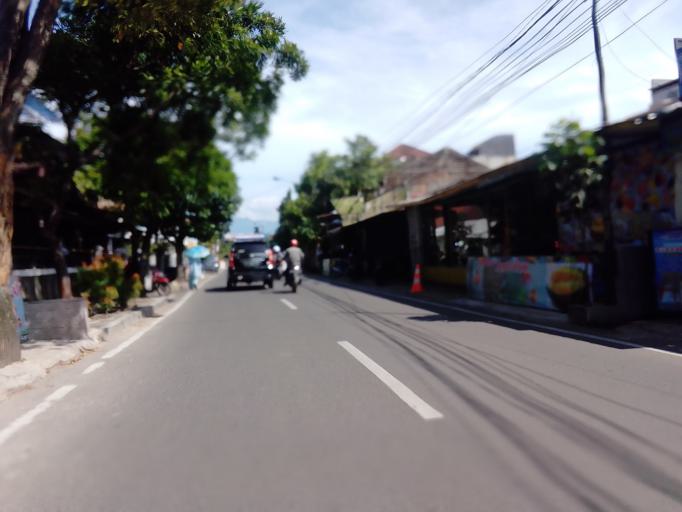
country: ID
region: West Java
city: Bandung
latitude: -6.9455
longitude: 107.6669
